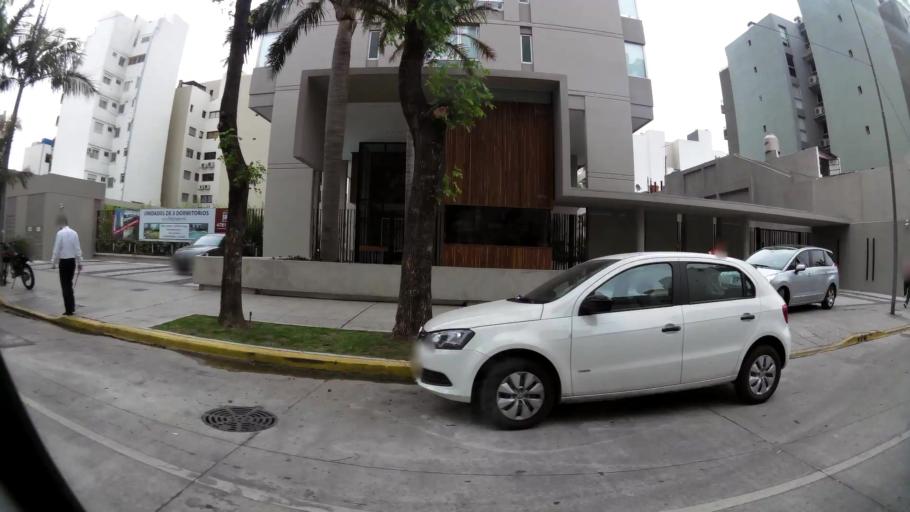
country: AR
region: Buenos Aires F.D.
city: Colegiales
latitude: -34.5527
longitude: -58.4571
